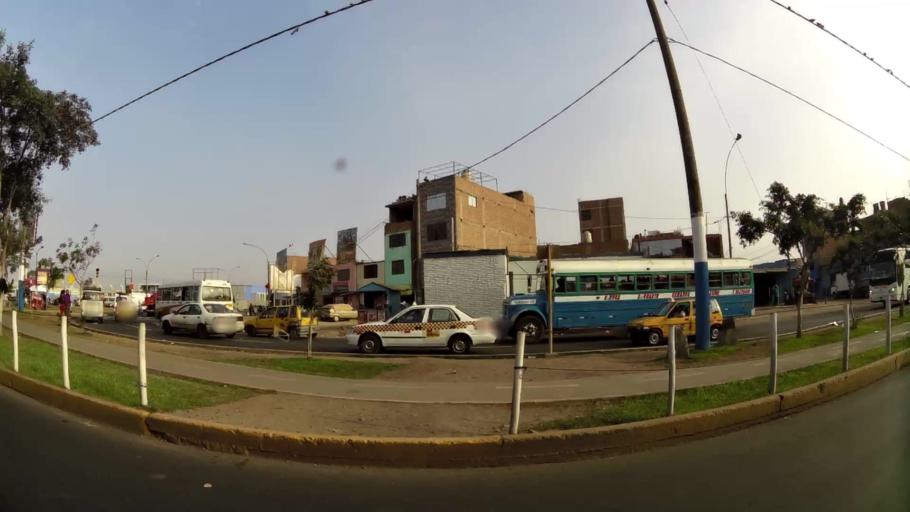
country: PE
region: Lima
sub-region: Lima
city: Independencia
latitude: -12.0258
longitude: -77.0760
